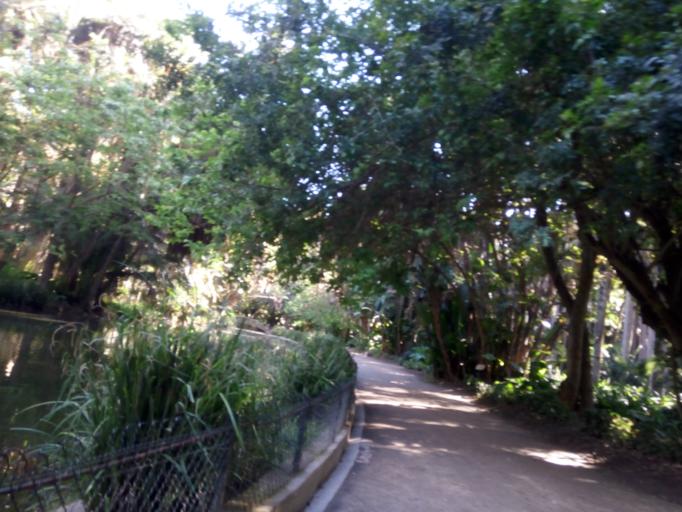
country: DZ
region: Alger
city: Algiers
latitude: 36.7471
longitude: 3.0776
